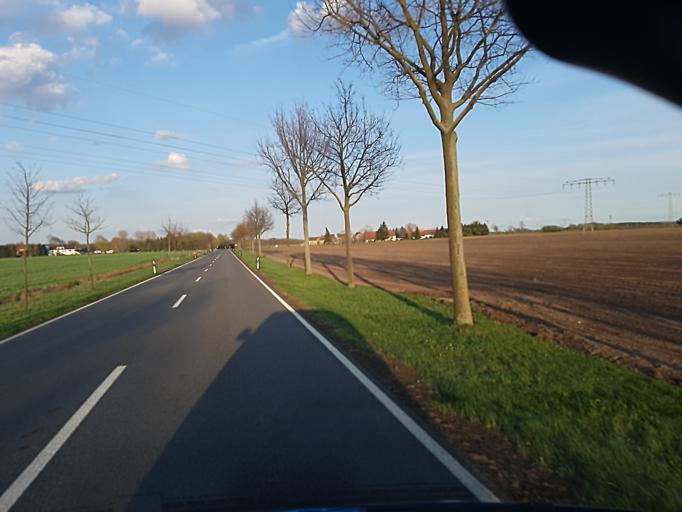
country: DE
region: Saxony
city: Trossin
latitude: 51.5652
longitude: 12.8360
